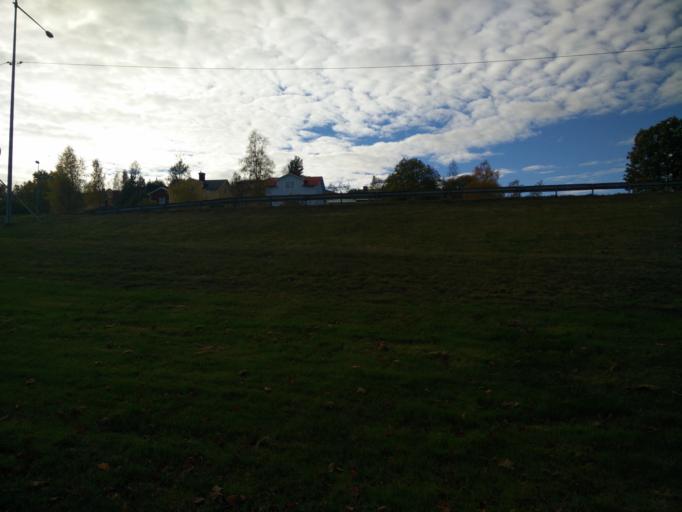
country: SE
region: Vaesternorrland
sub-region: Haernoesands Kommun
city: Haernoesand
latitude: 62.6324
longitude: 17.9290
